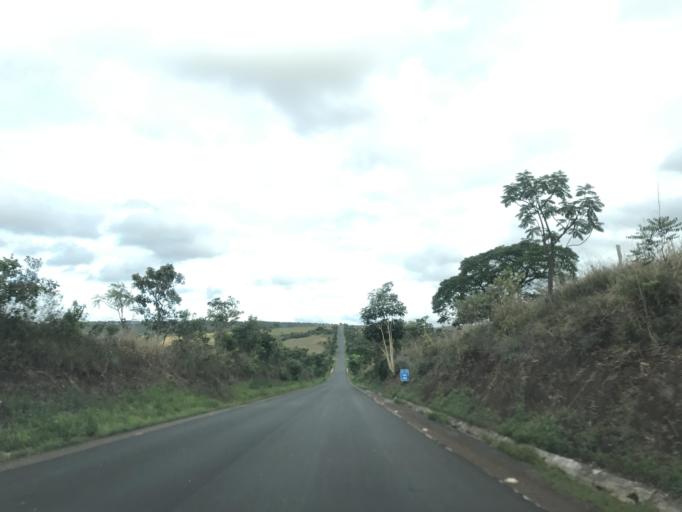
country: BR
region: Goias
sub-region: Vianopolis
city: Vianopolis
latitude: -16.9470
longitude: -48.5849
